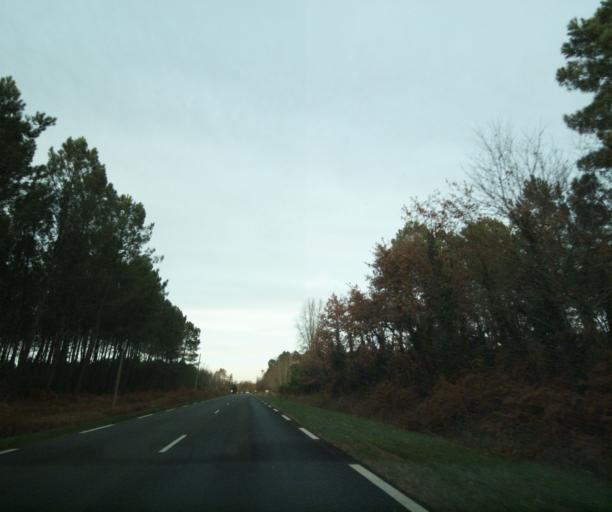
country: FR
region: Aquitaine
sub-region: Departement de la Gironde
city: Bazas
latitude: 44.3326
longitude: -0.2366
